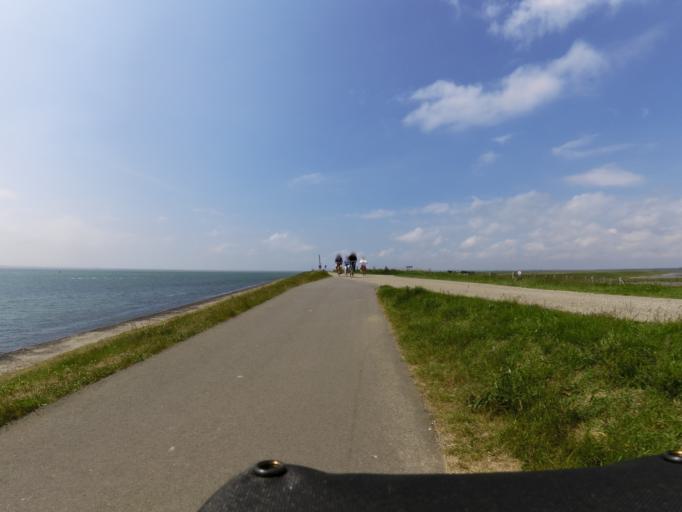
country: NL
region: Zeeland
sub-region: Schouwen-Duiveland
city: Scharendijke
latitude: 51.6780
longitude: 3.8553
